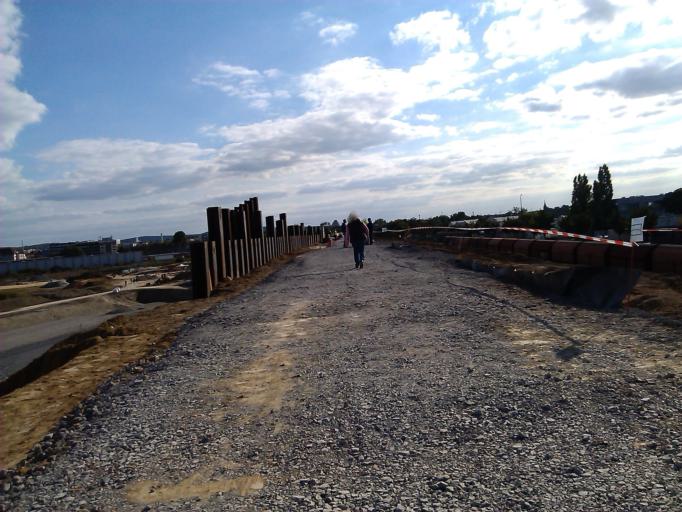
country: DE
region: Baden-Wuerttemberg
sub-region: Regierungsbezirk Stuttgart
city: Heilbronn
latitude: 49.1483
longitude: 9.2056
